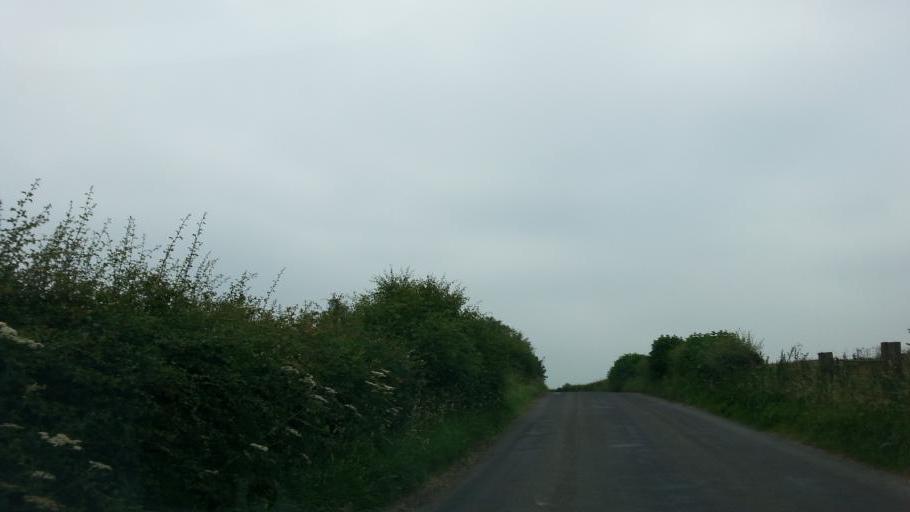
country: GB
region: England
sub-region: Staffordshire
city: Rugeley
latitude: 52.8299
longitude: -1.9052
